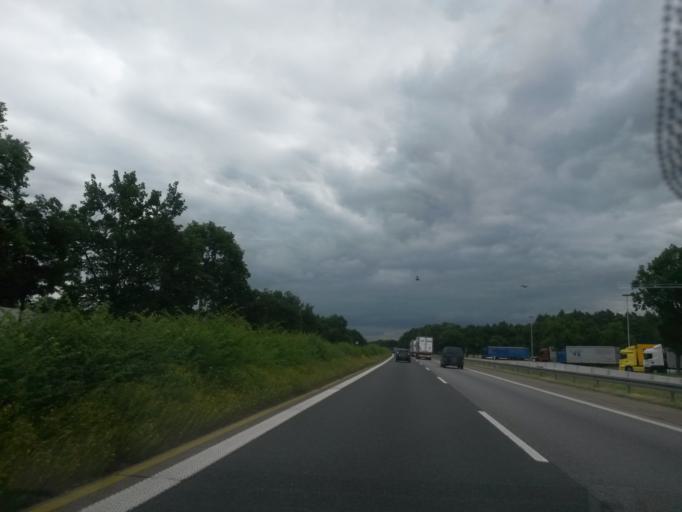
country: DE
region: Bavaria
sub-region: Regierungsbezirk Mittelfranken
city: Wachenroth
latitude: 49.7313
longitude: 10.7264
